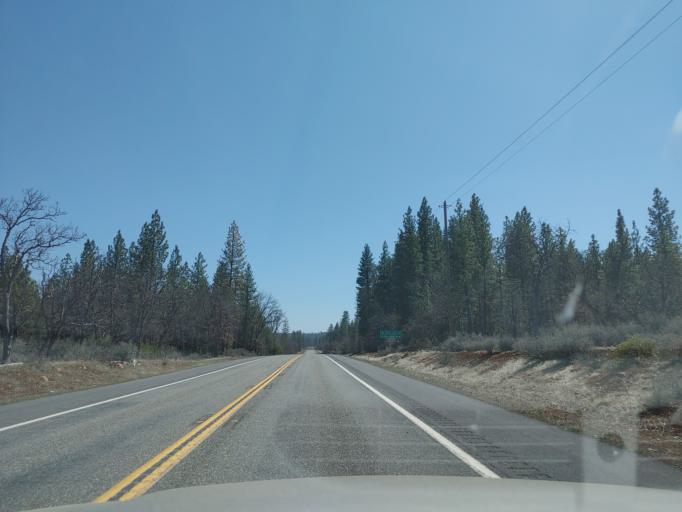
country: US
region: California
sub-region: Shasta County
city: Burney
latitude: 41.0525
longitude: -121.6396
